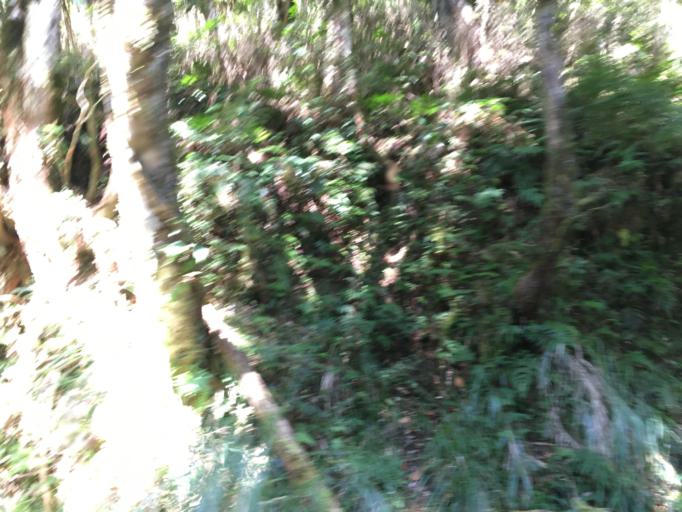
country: TW
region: Taiwan
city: Daxi
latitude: 24.5674
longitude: 121.4142
